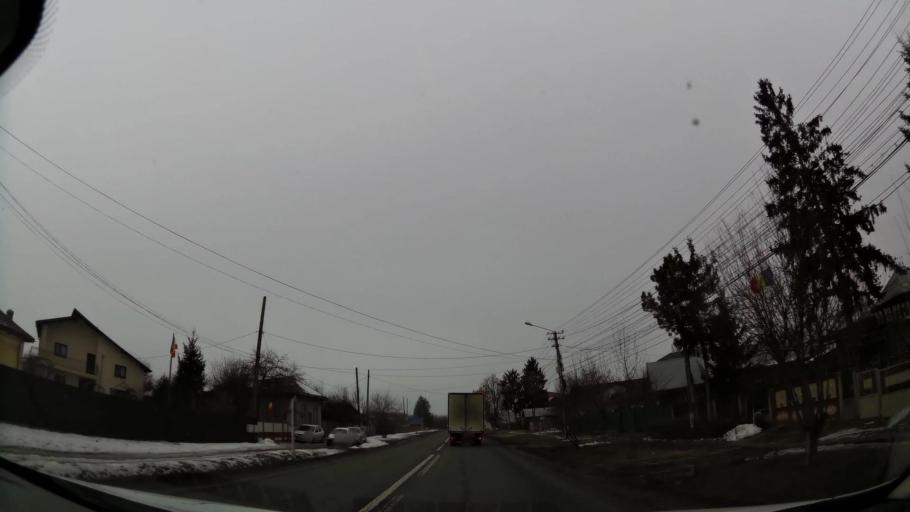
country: RO
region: Dambovita
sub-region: Comuna Racari
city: Racari
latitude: 44.6295
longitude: 25.7323
